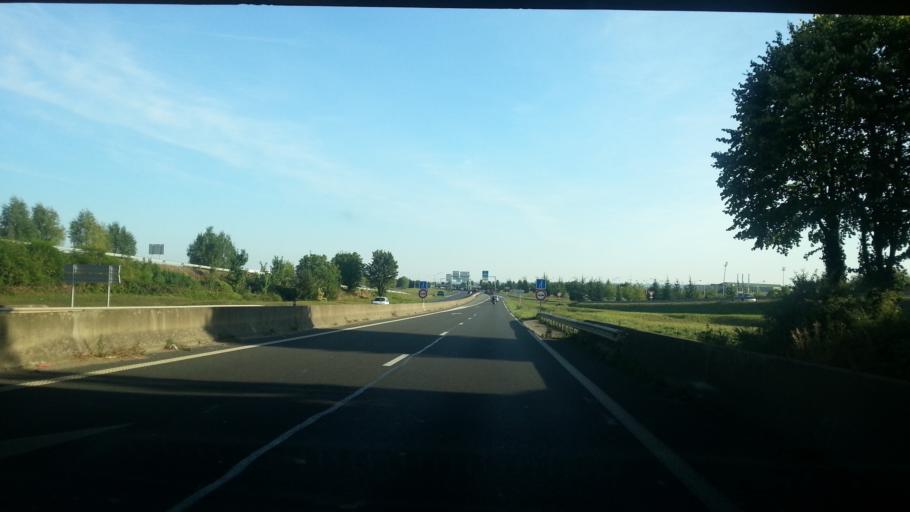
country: FR
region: Picardie
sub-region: Departement de l'Oise
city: Tille
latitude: 49.4386
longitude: 2.1141
